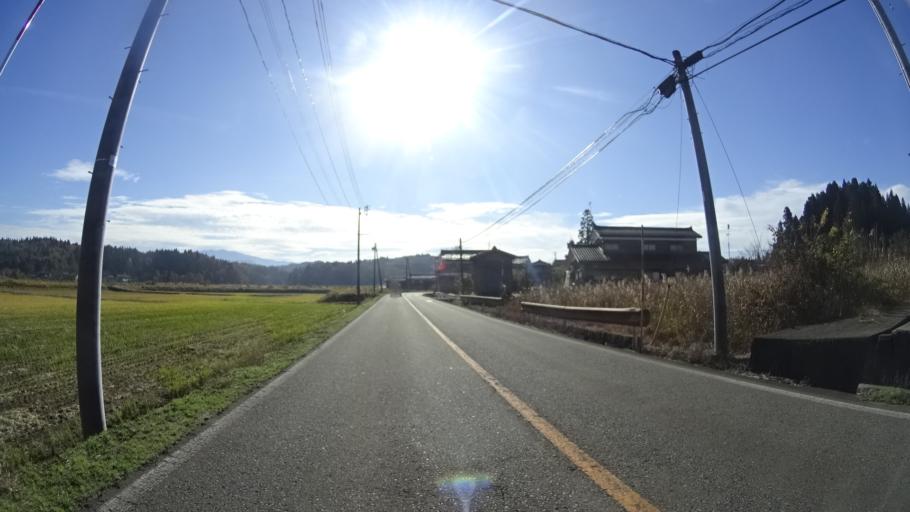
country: JP
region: Niigata
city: Tochio-honcho
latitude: 37.5019
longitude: 138.9732
